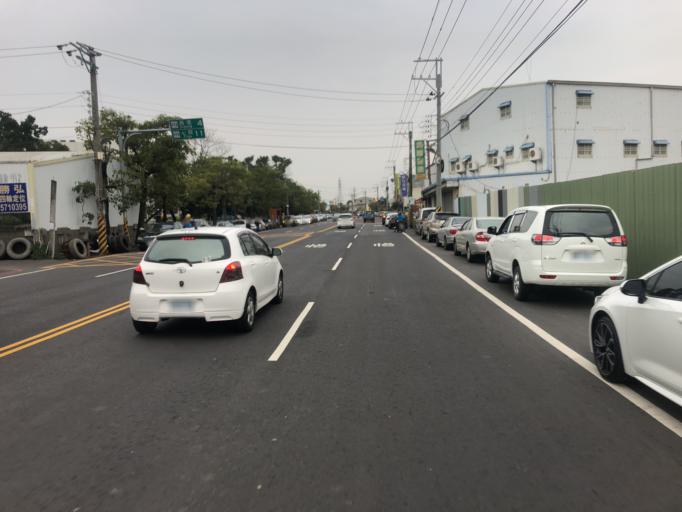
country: TW
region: Taiwan
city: Xinying
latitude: 23.1749
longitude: 120.2466
